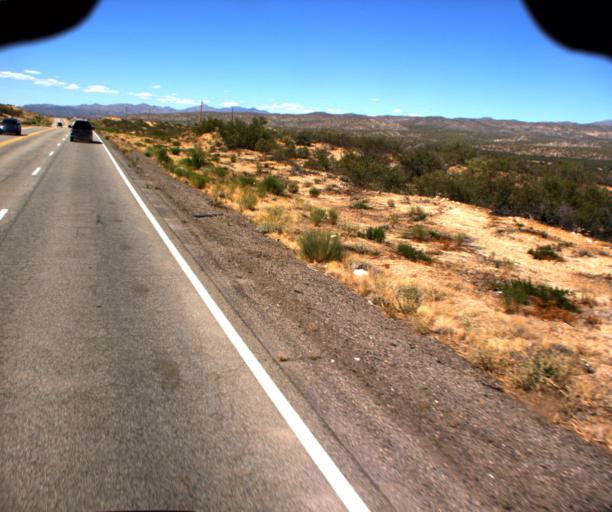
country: US
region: Arizona
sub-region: Yavapai County
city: Bagdad
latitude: 34.8085
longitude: -113.6259
